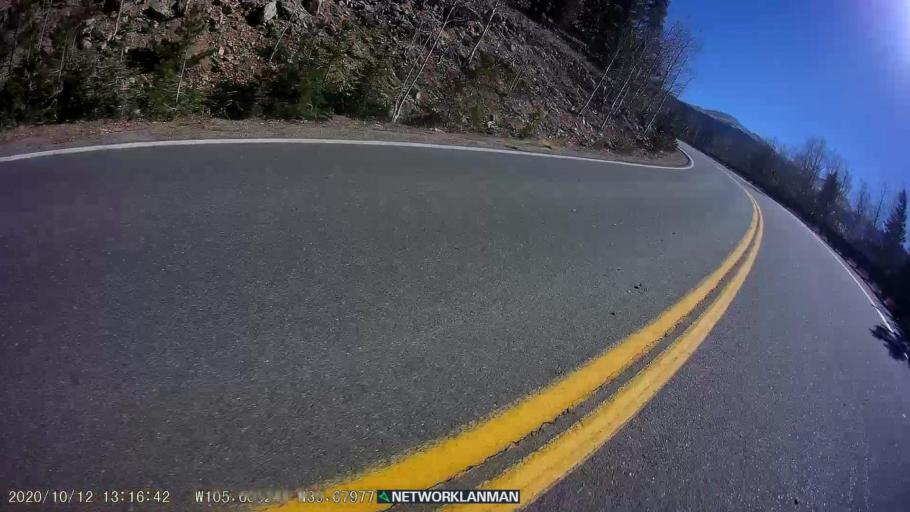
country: US
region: Colorado
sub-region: Clear Creek County
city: Georgetown
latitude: 39.6795
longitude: -105.6054
